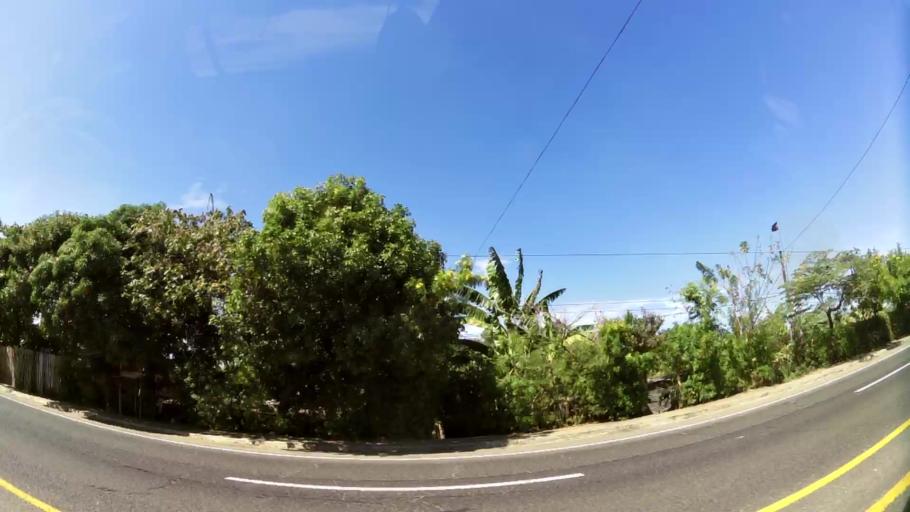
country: SV
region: Ahuachapan
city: Atiquizaya
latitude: 13.9698
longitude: -89.7533
